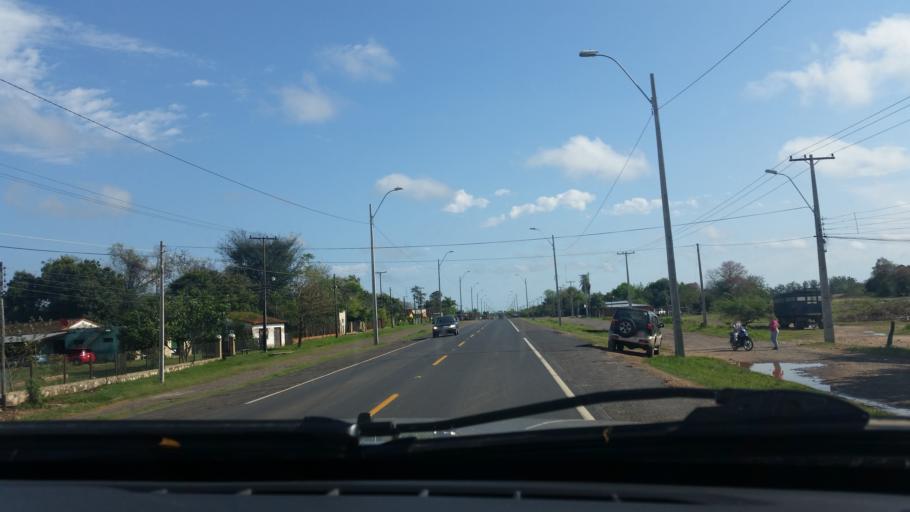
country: PY
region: Presidente Hayes
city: Benjamin Aceval
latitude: -24.9542
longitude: -57.5499
